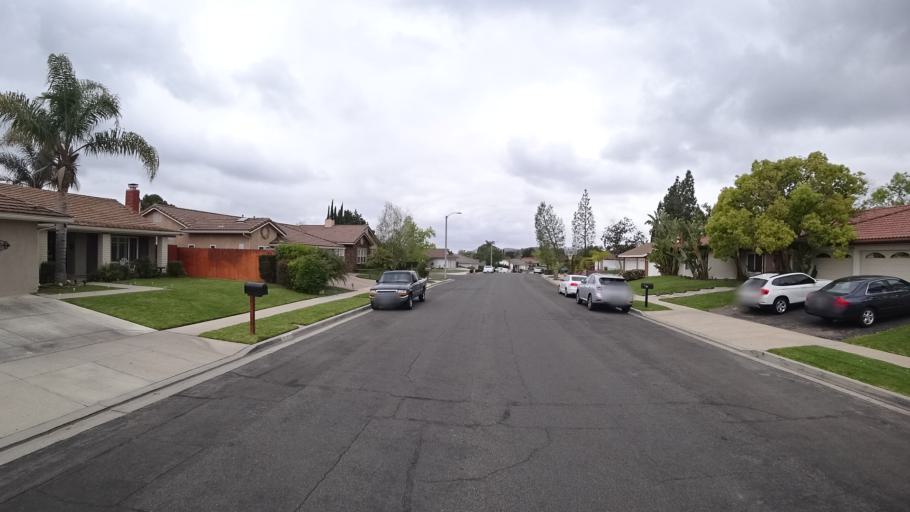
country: US
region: California
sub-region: Ventura County
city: Thousand Oaks
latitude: 34.2168
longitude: -118.8722
